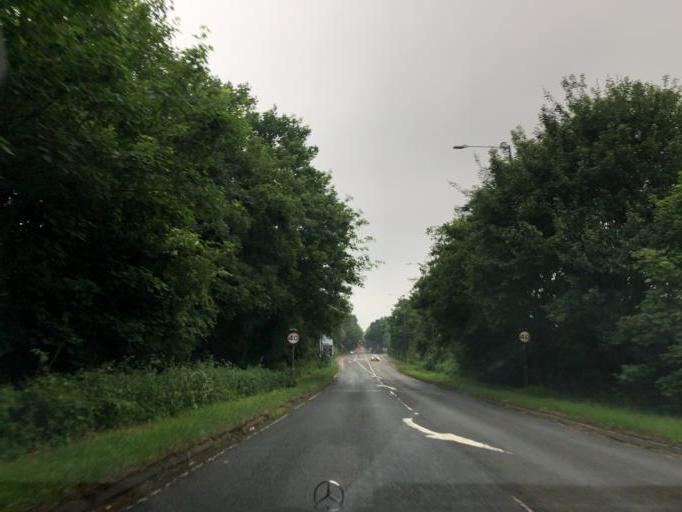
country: GB
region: England
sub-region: Warwickshire
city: Warwick
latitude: 52.2725
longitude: -1.5718
